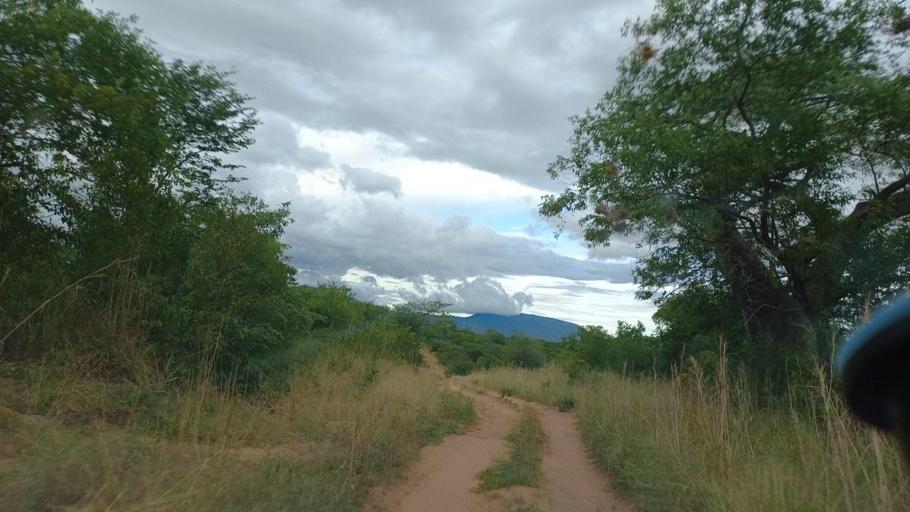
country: ZM
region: Lusaka
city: Luangwa
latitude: -15.5642
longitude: 30.3391
